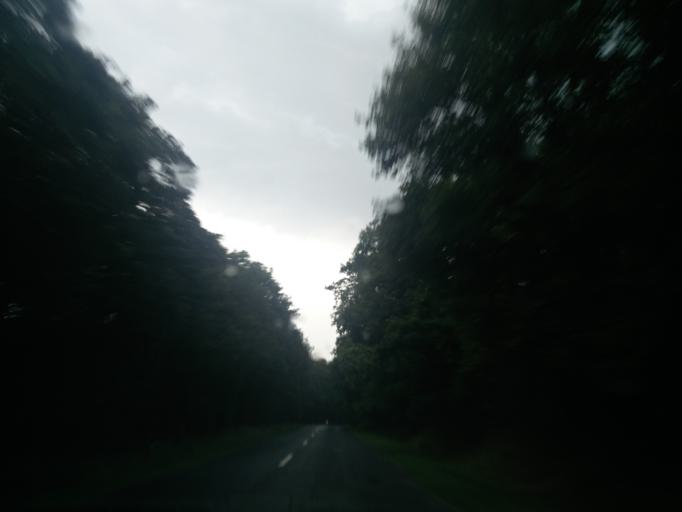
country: HU
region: Fejer
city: Lovasbereny
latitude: 47.2816
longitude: 18.5819
